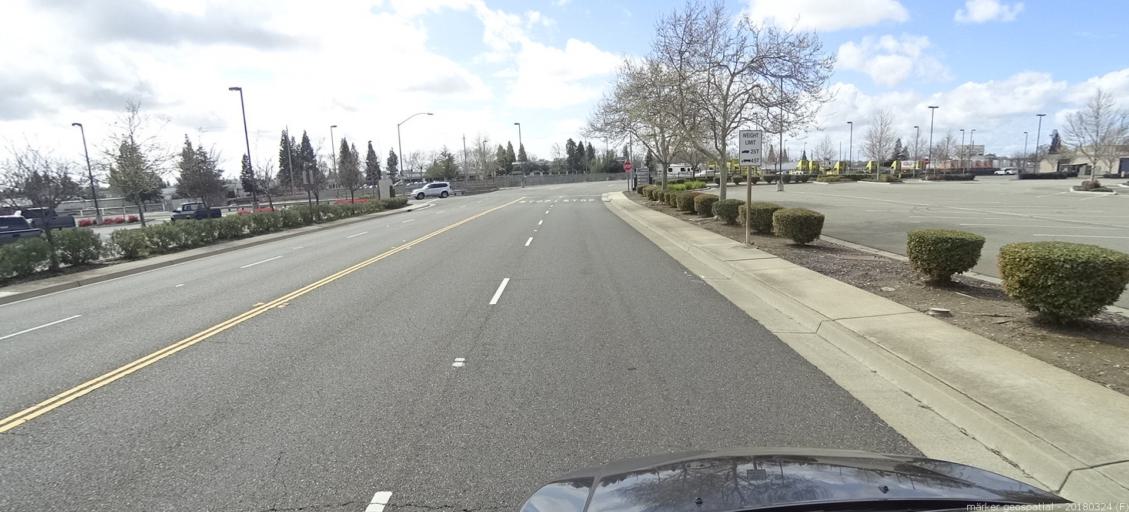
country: US
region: California
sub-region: Sacramento County
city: North Highlands
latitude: 38.6565
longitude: -121.3882
